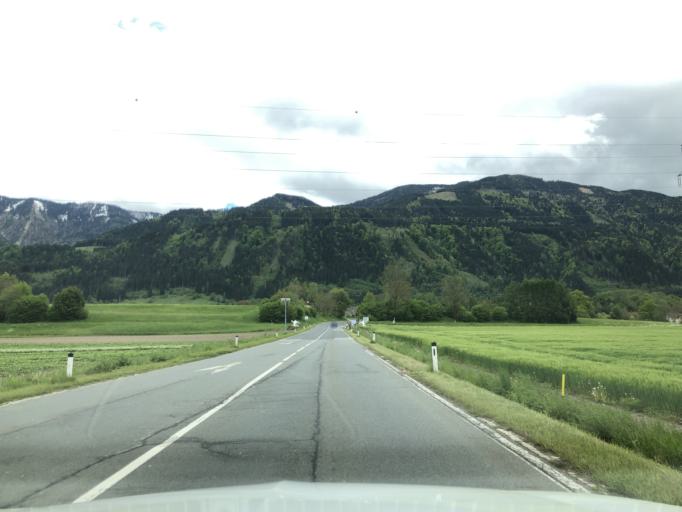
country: AT
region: Carinthia
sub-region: Politischer Bezirk Villach Land
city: Arnoldstein
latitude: 46.5534
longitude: 13.7879
